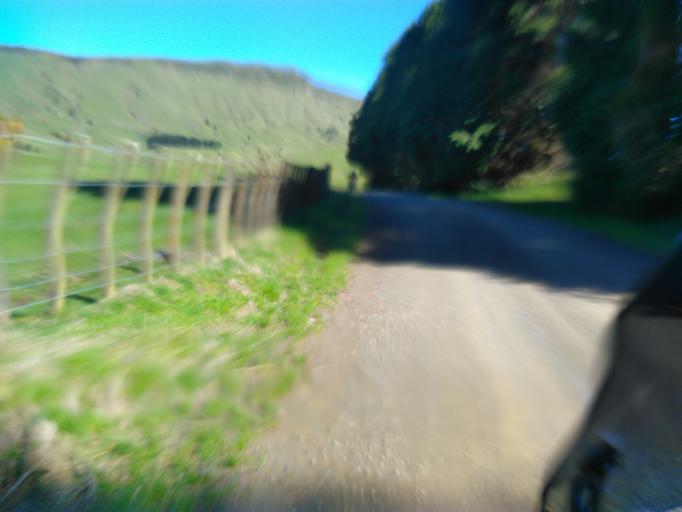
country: NZ
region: Bay of Plenty
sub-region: Opotiki District
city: Opotiki
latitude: -38.3116
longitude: 177.5667
